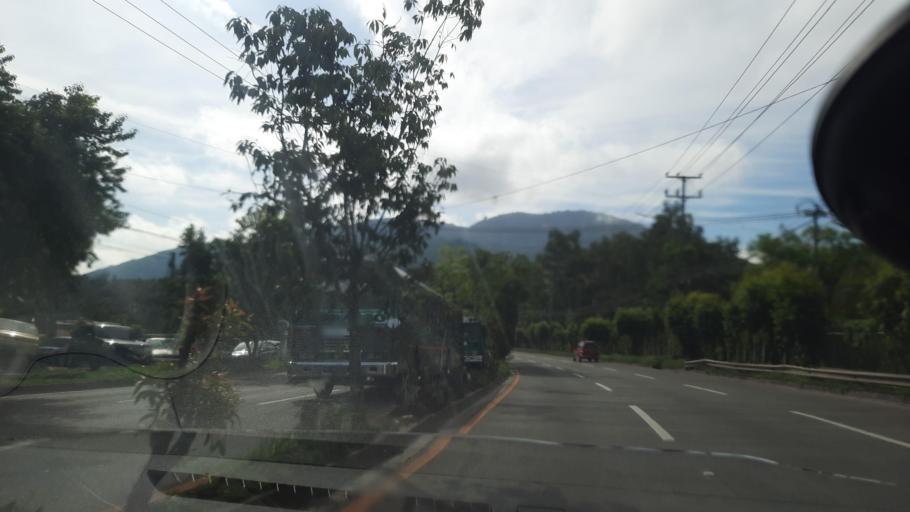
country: SV
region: San Salvador
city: San Salvador
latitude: 13.6745
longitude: -89.2038
